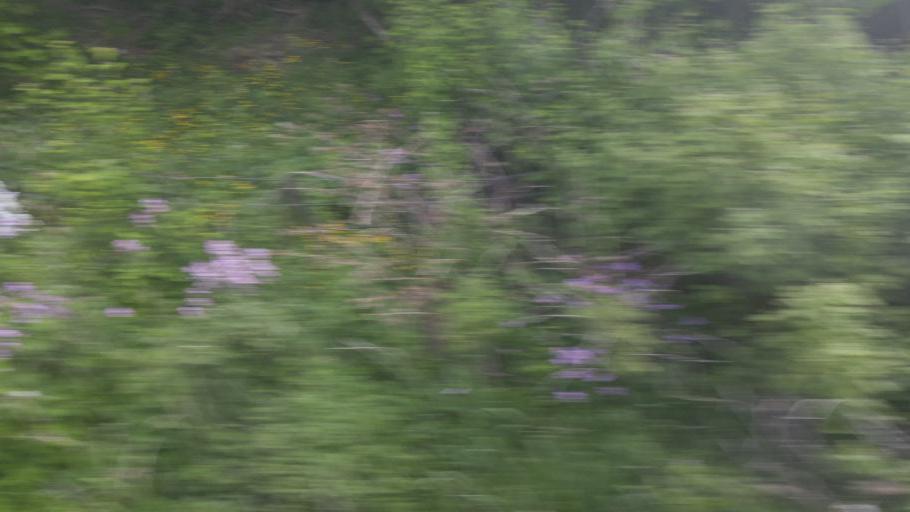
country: NO
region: Sor-Trondelag
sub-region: Melhus
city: Melhus
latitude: 63.2219
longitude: 10.2997
